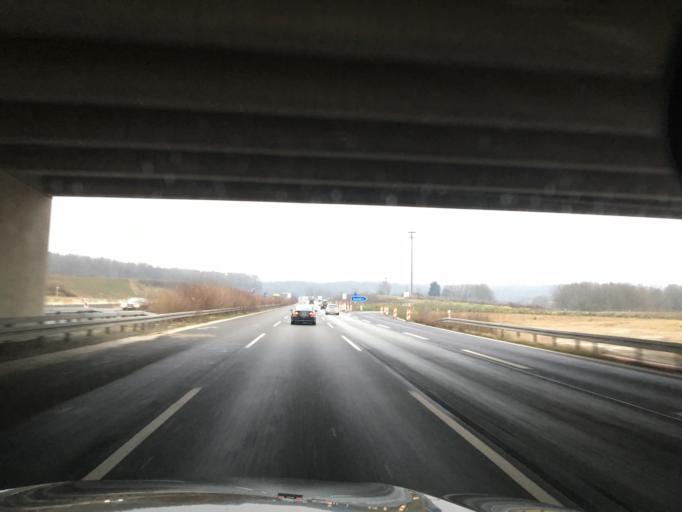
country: DE
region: Bavaria
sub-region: Regierungsbezirk Unterfranken
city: Reichenberg
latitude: 49.7528
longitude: 9.9285
